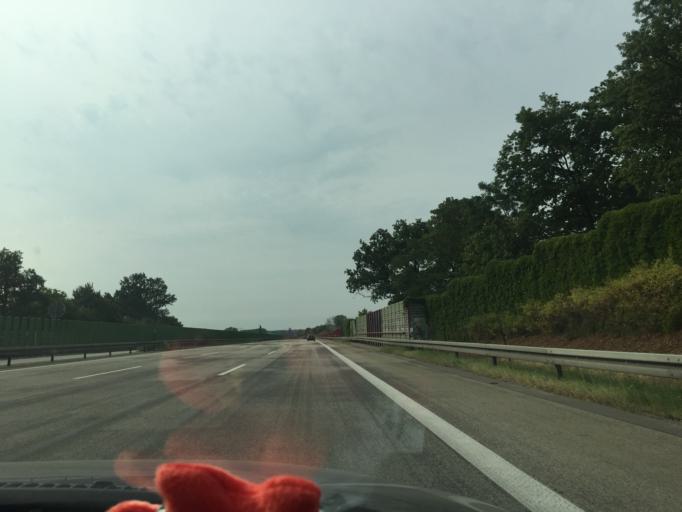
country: DE
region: Brandenburg
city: Woltersdorf
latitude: 52.4659
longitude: 13.7862
